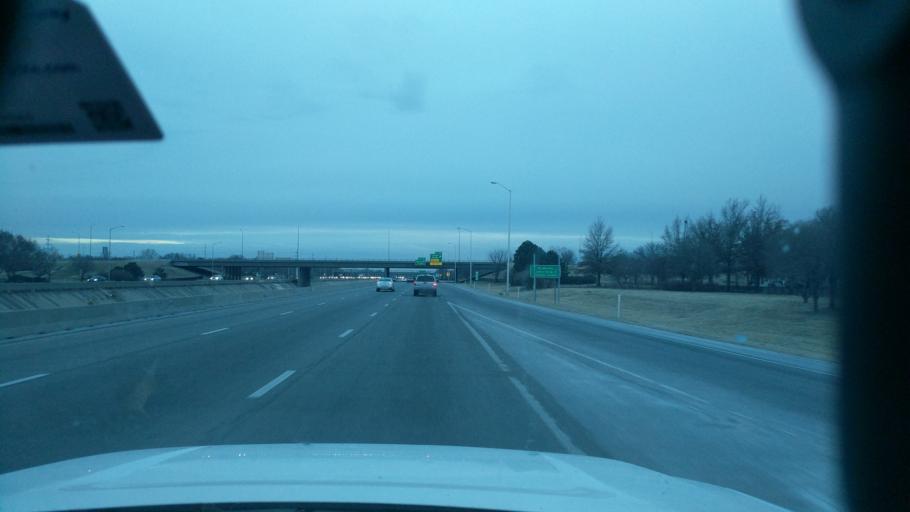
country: US
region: Kansas
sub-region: Sedgwick County
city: Wichita
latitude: 37.6740
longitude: -97.3130
